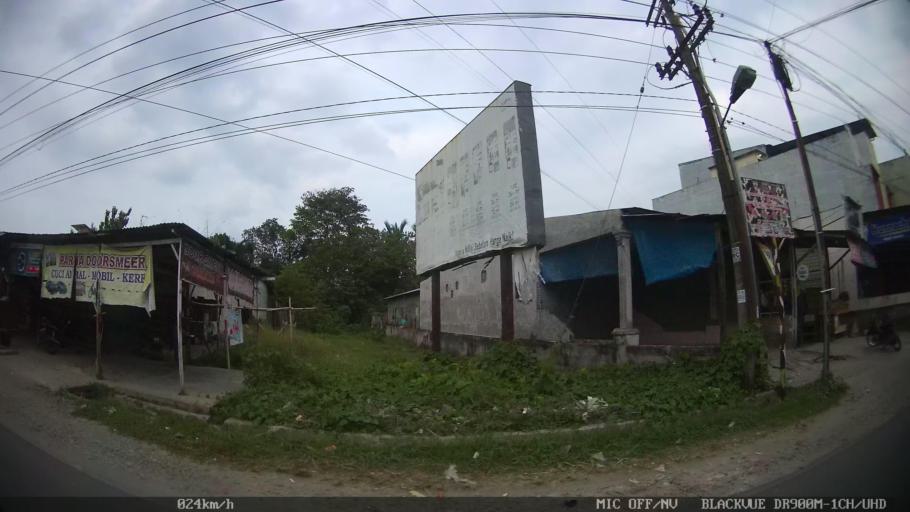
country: ID
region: North Sumatra
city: Sunggal
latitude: 3.5756
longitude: 98.5877
